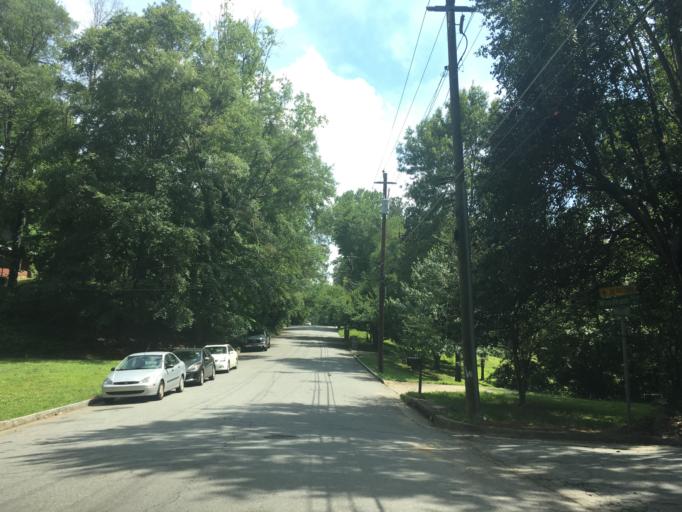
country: US
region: Georgia
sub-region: DeKalb County
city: Druid Hills
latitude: 33.8075
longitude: -84.3601
